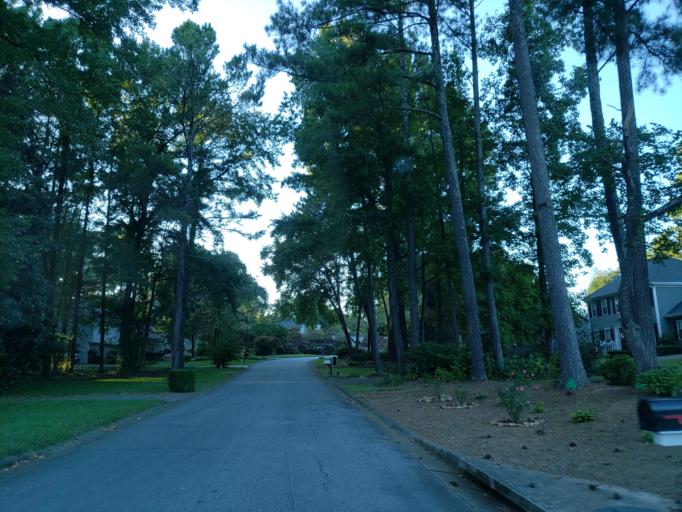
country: US
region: Georgia
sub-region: Cobb County
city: Kennesaw
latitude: 34.0312
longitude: -84.5892
